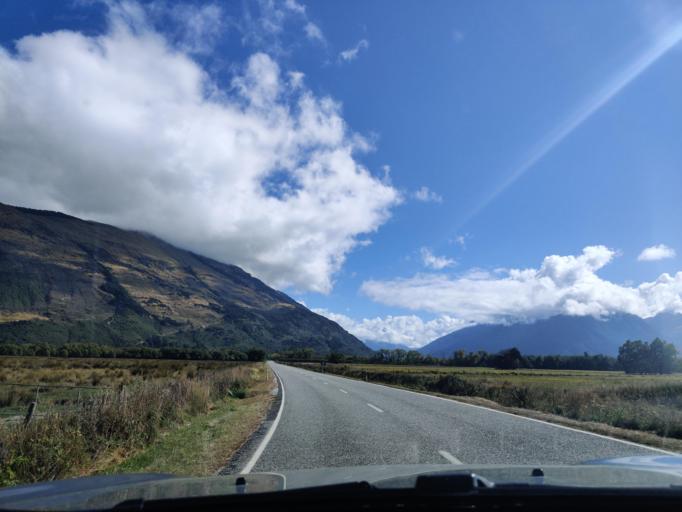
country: NZ
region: Otago
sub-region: Queenstown-Lakes District
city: Queenstown
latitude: -44.7938
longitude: 168.4024
